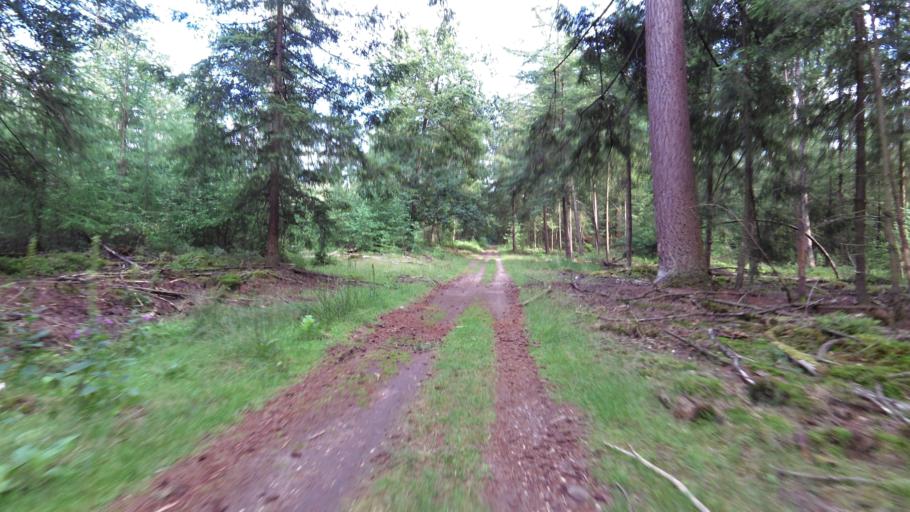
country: NL
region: Gelderland
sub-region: Gemeente Apeldoorn
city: Uddel
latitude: 52.2364
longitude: 5.8741
